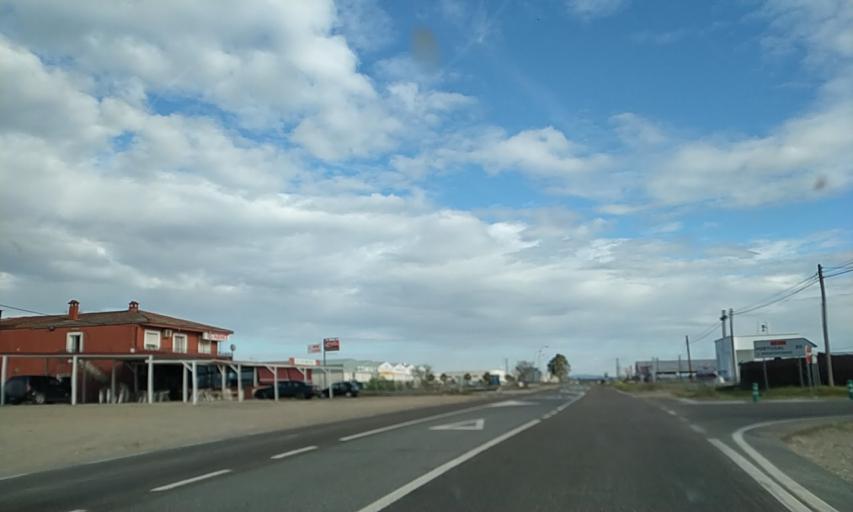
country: ES
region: Extremadura
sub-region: Provincia de Caceres
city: Moraleja
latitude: 40.0606
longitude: -6.6488
